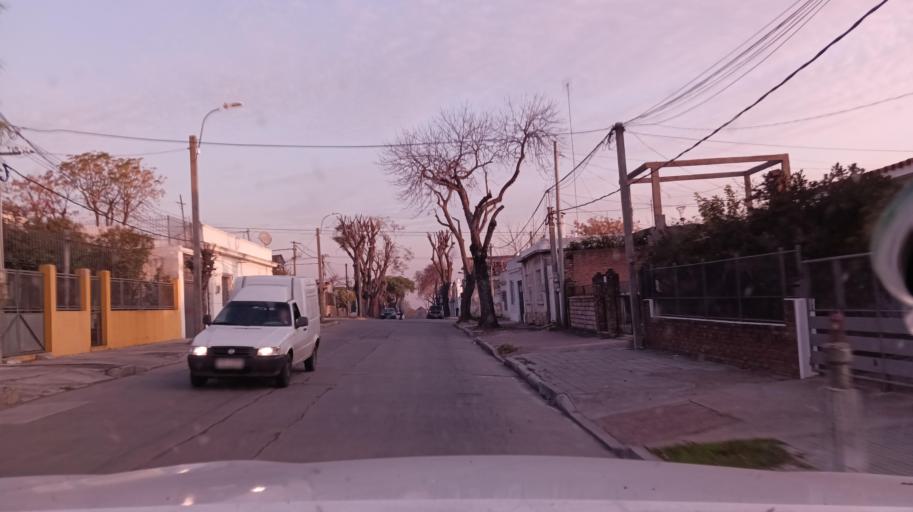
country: UY
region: Montevideo
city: Montevideo
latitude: -34.8562
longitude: -56.1727
